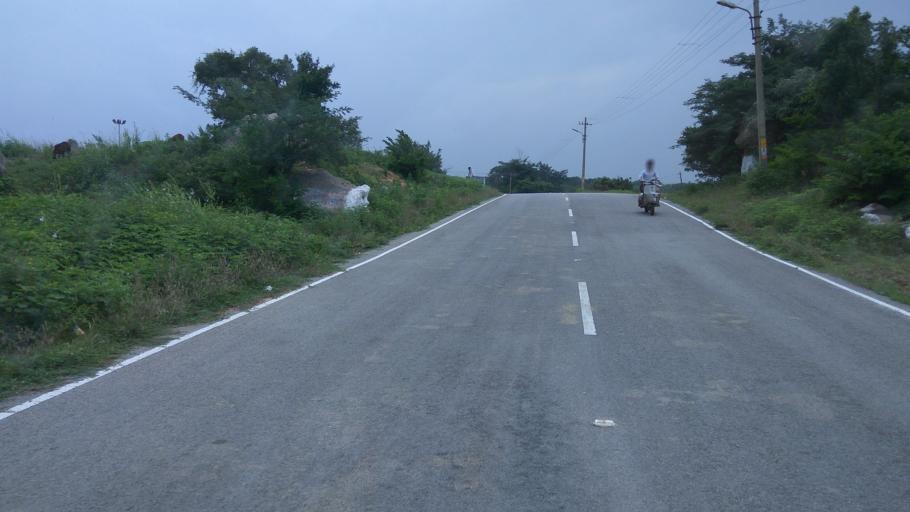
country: IN
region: Telangana
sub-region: Rangareddi
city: Ghatkesar
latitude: 17.5365
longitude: 78.6930
